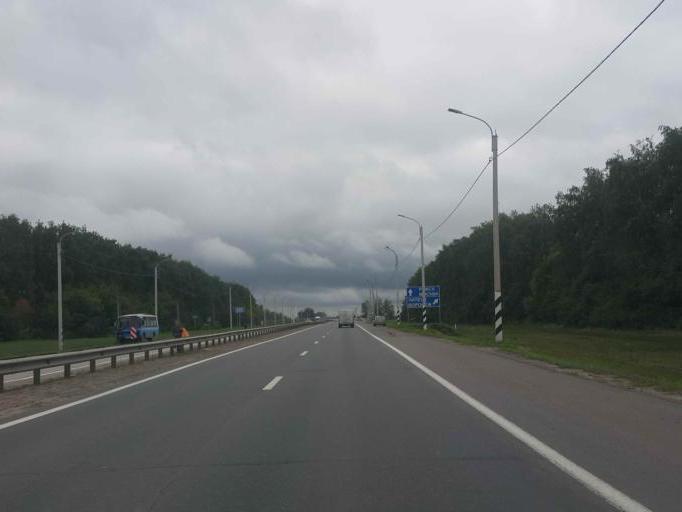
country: RU
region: Tambov
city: Komsomolets
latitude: 52.7368
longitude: 41.2623
